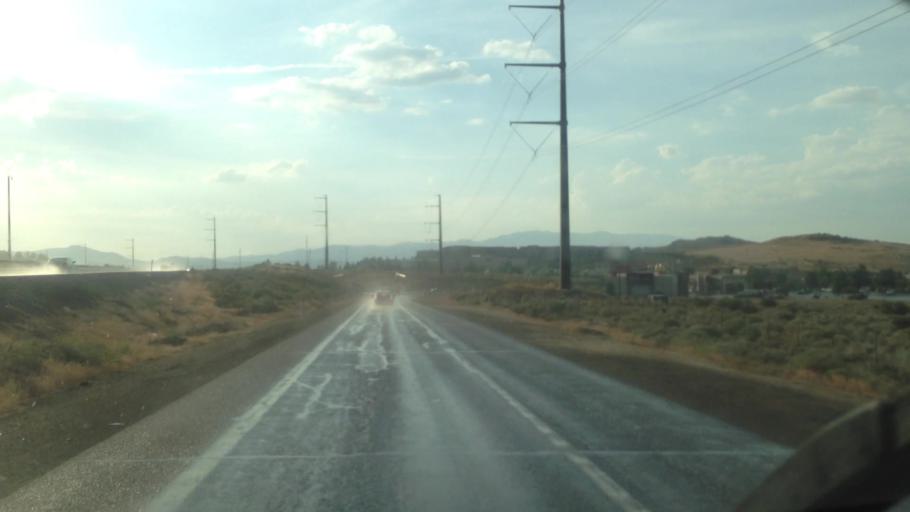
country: US
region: Nevada
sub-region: Washoe County
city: Golden Valley
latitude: 39.6095
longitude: -119.8477
